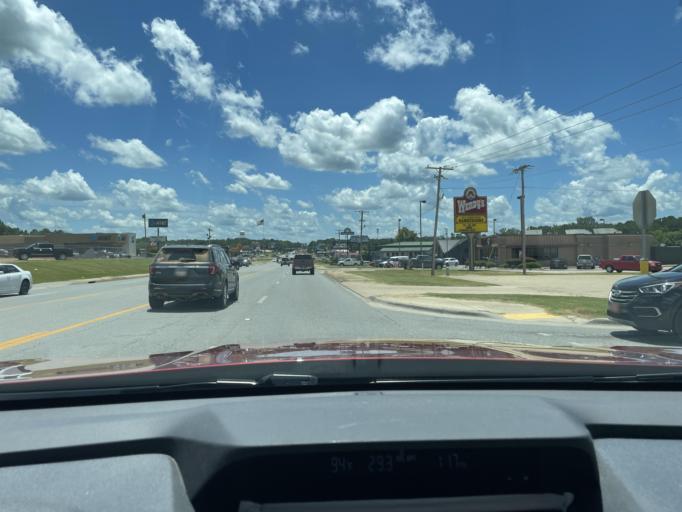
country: US
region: Arkansas
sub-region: Drew County
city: Monticello
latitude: 33.6353
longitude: -91.8018
